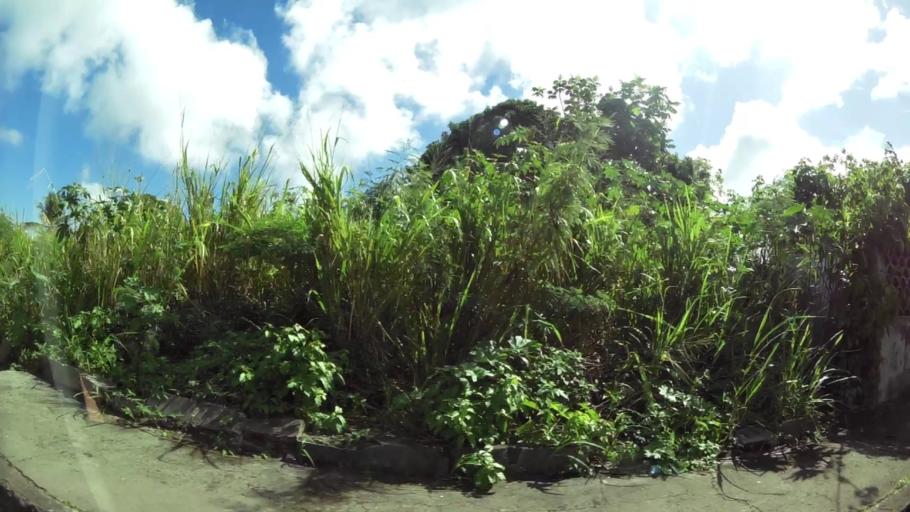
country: GP
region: Guadeloupe
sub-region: Guadeloupe
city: Anse-Bertrand
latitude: 16.4727
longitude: -61.5067
